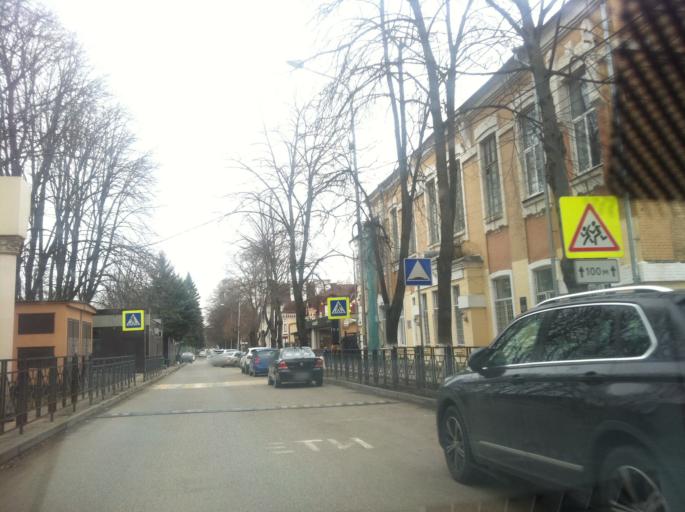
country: RU
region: Stavropol'skiy
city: Svobody
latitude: 44.0354
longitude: 43.0581
